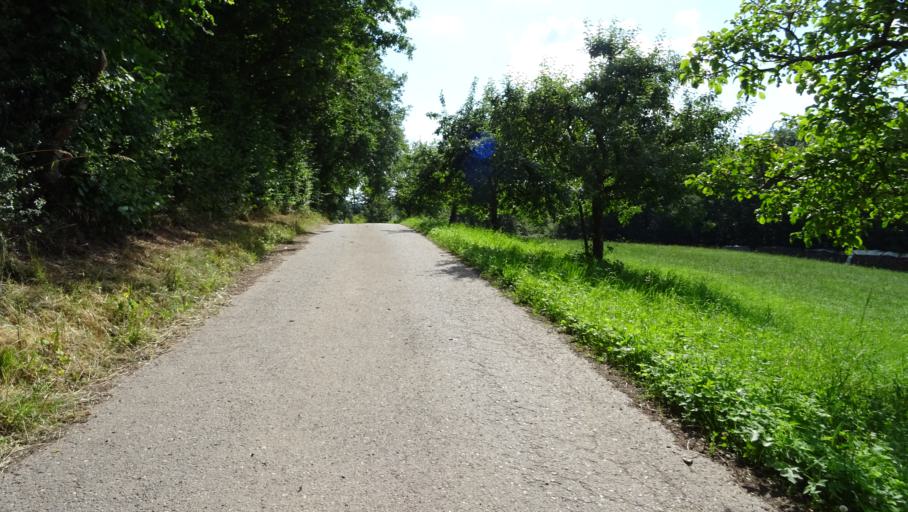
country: DE
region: Baden-Wuerttemberg
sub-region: Karlsruhe Region
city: Limbach
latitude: 49.4295
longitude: 9.2383
